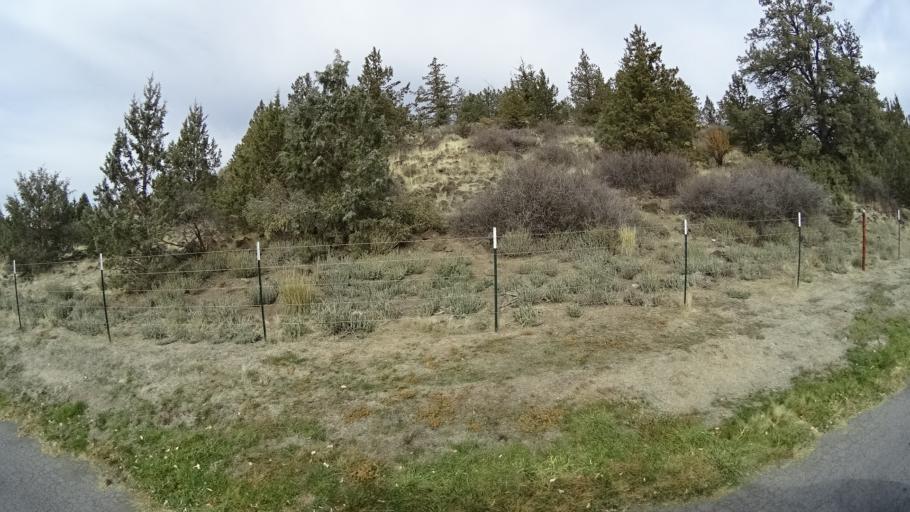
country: US
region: California
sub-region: Siskiyou County
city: Montague
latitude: 41.6823
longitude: -122.5255
